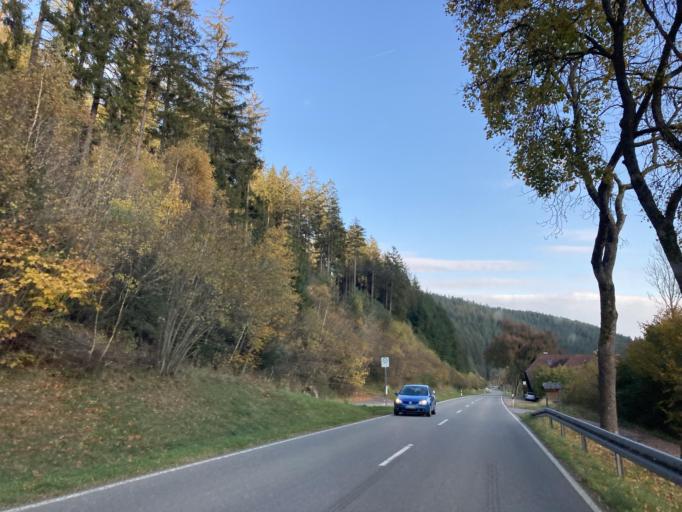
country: DE
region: Baden-Wuerttemberg
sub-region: Freiburg Region
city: Vohrenbach
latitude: 48.0070
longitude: 8.2924
